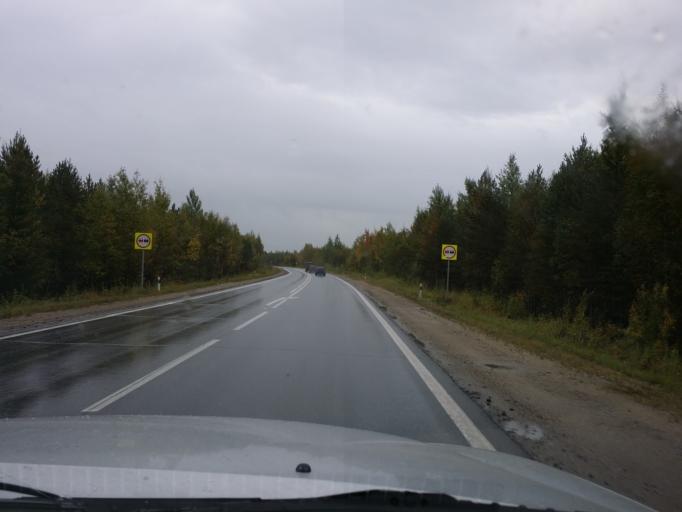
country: RU
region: Khanty-Mansiyskiy Avtonomnyy Okrug
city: Langepas
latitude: 61.1595
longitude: 75.6003
